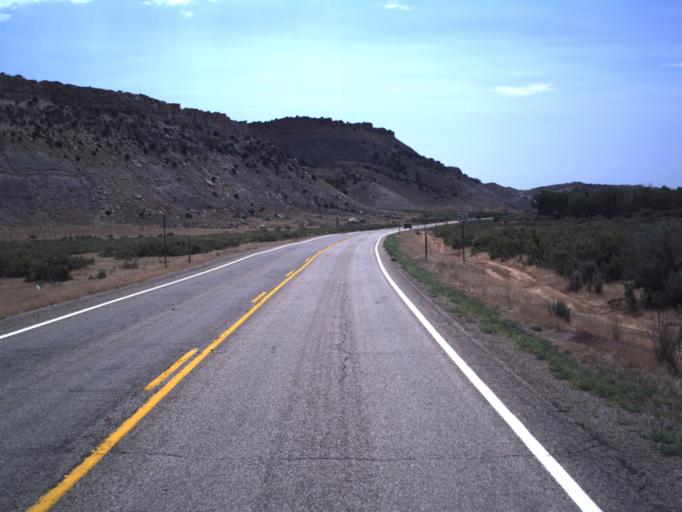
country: US
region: Utah
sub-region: Uintah County
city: Vernal
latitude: 40.5360
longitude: -109.5228
